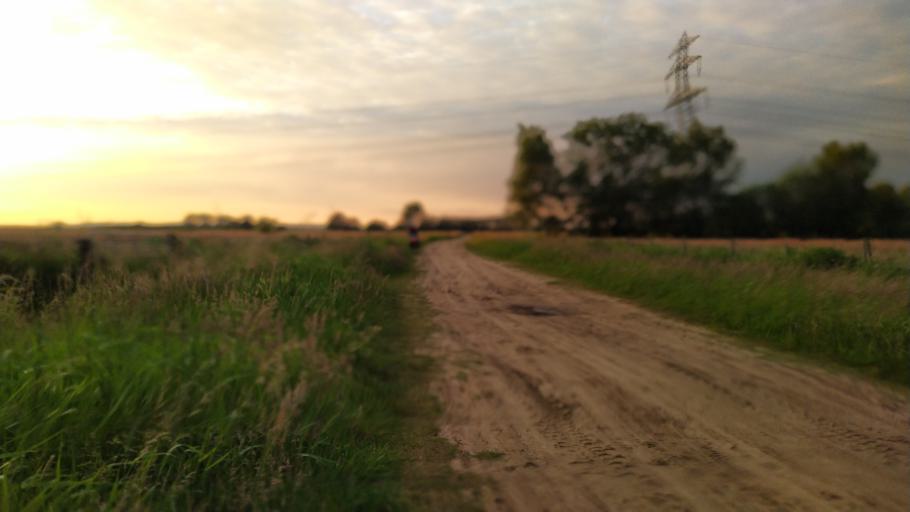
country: DE
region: Lower Saxony
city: Neu Wulmstorf
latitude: 53.4915
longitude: 9.8267
